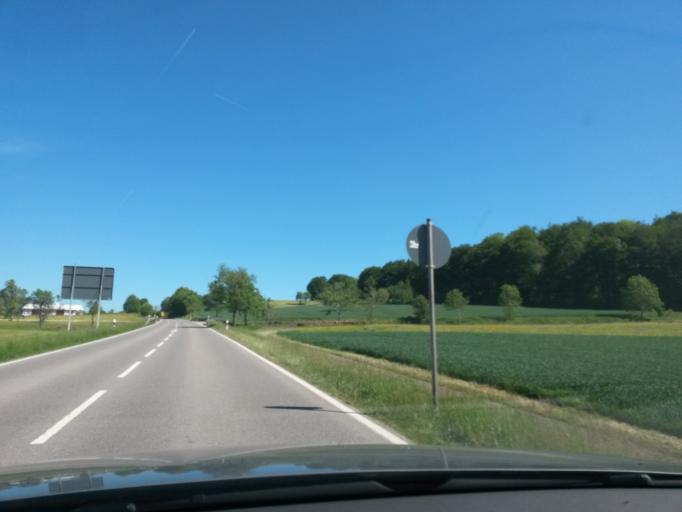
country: DE
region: Baden-Wuerttemberg
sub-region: Tuebingen Region
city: Trochtelfingen
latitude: 48.2679
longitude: 9.2796
